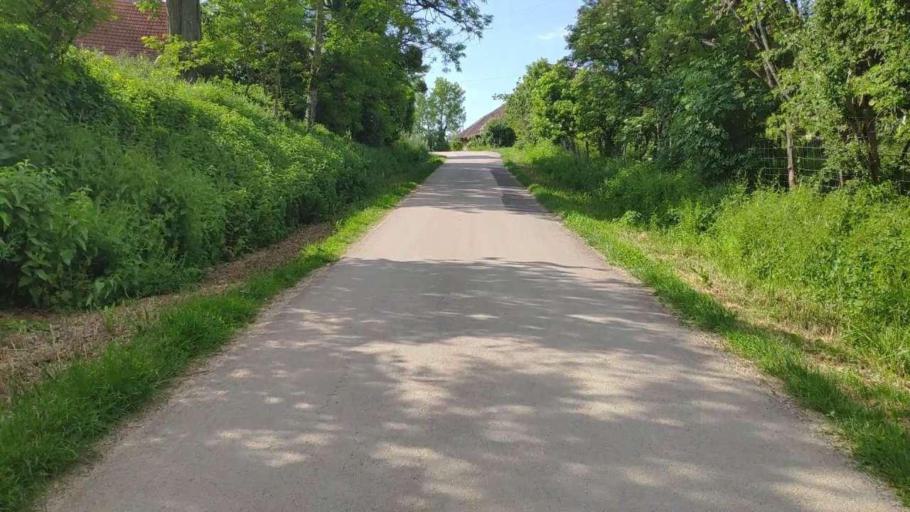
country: FR
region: Franche-Comte
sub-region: Departement du Jura
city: Bletterans
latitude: 46.8198
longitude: 5.3665
